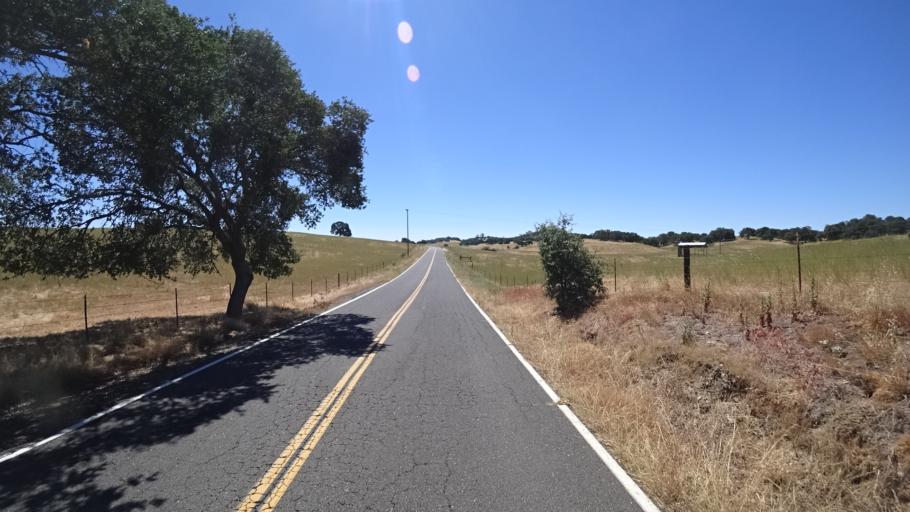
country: US
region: California
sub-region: Calaveras County
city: Copperopolis
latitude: 38.0231
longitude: -120.7164
